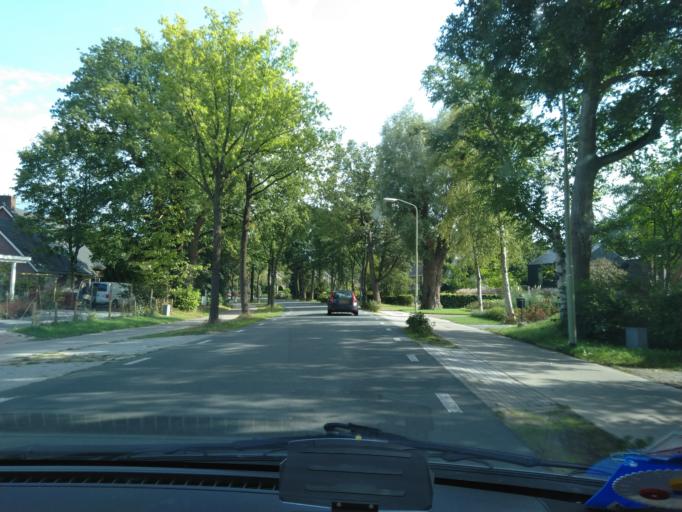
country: NL
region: Groningen
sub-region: Gemeente Groningen
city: Groningen
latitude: 53.1709
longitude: 6.5487
